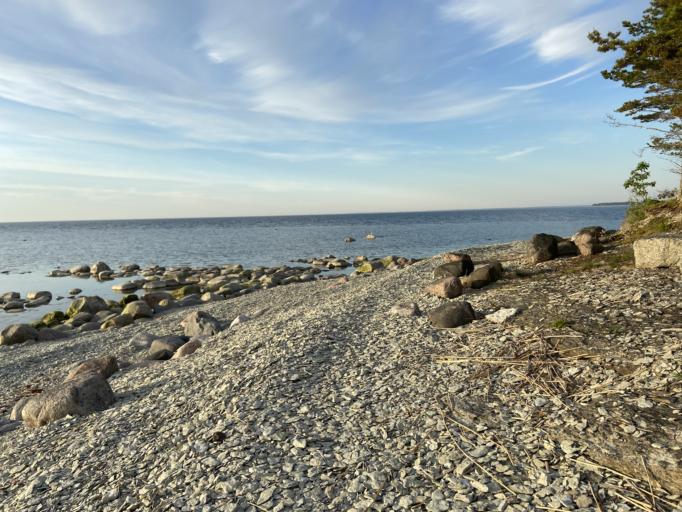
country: EE
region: Harju
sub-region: Paldiski linn
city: Paldiski
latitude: 59.2736
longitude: 23.7317
